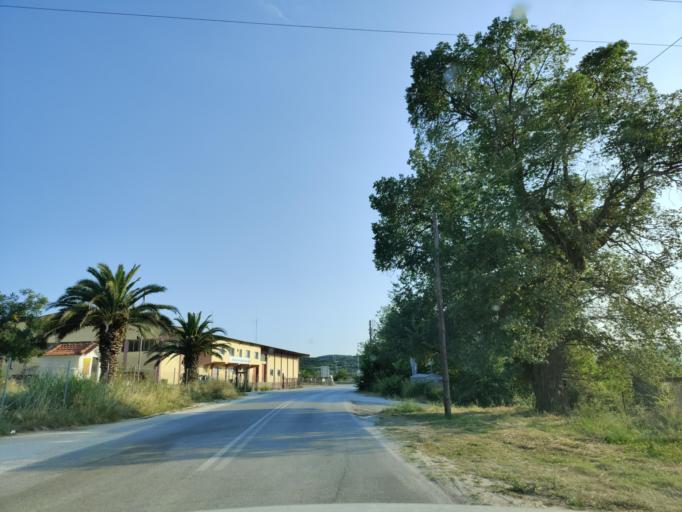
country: GR
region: East Macedonia and Thrace
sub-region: Nomos Kavalas
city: Nea Peramos
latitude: 40.8248
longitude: 24.2877
